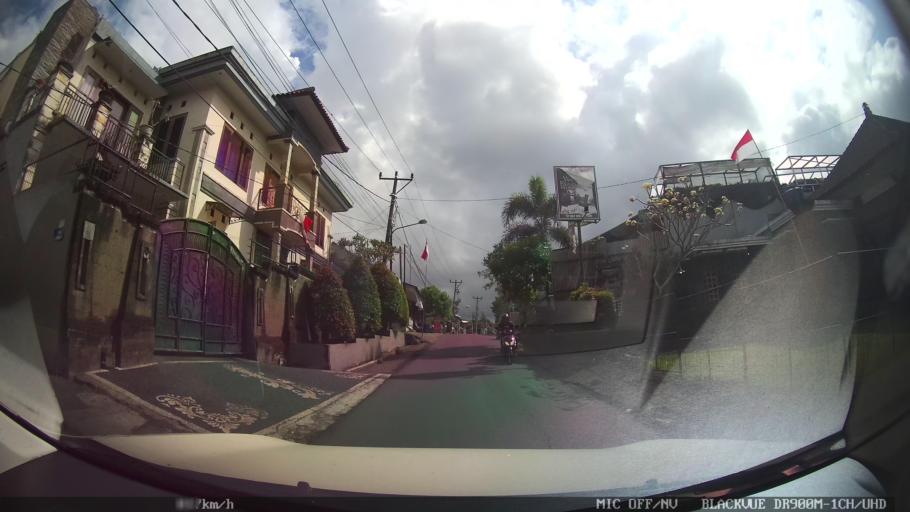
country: ID
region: Bali
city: Banjar Karangsuling
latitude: -8.6097
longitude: 115.2029
